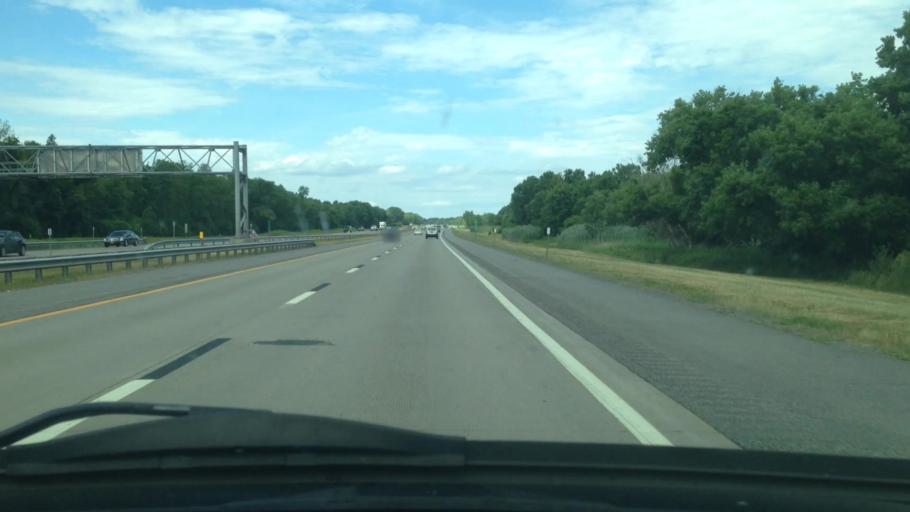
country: US
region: New York
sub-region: Onondaga County
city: Jordan
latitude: 43.0769
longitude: -76.4832
